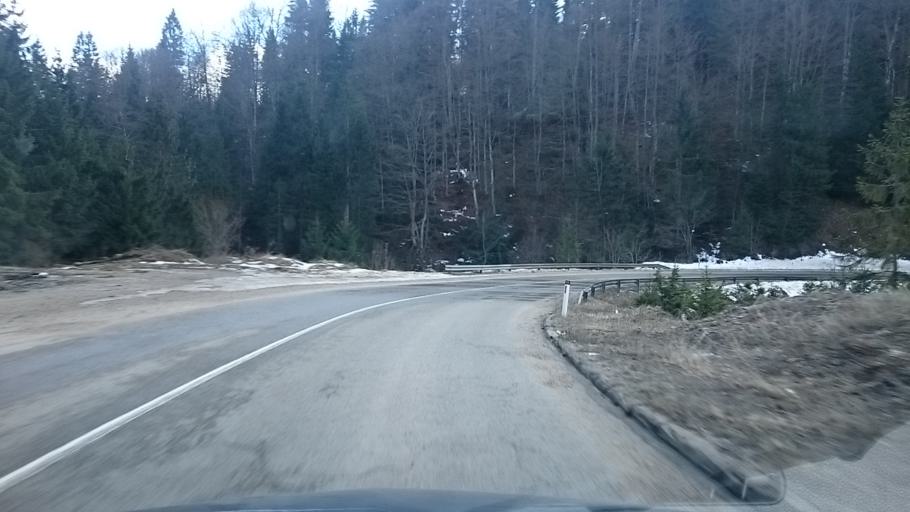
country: BA
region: Republika Srpska
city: Skender Vakuf
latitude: 44.4704
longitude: 17.3889
